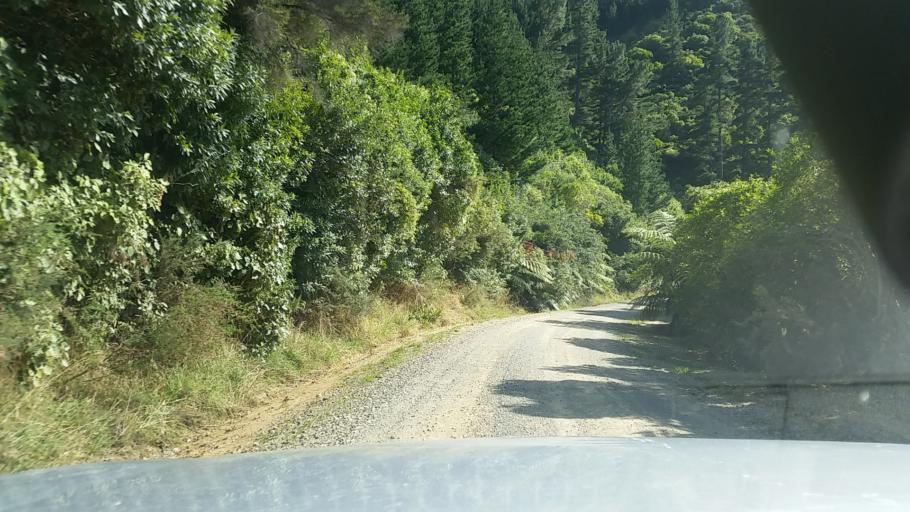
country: NZ
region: Marlborough
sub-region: Marlborough District
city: Picton
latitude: -41.2897
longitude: 174.1712
